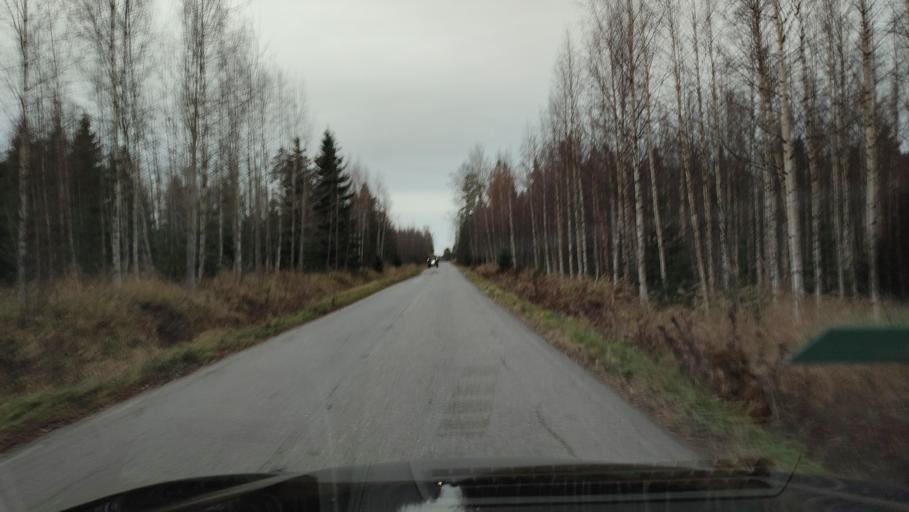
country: FI
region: Ostrobothnia
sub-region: Sydosterbotten
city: Naerpes
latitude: 62.4256
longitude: 21.4150
